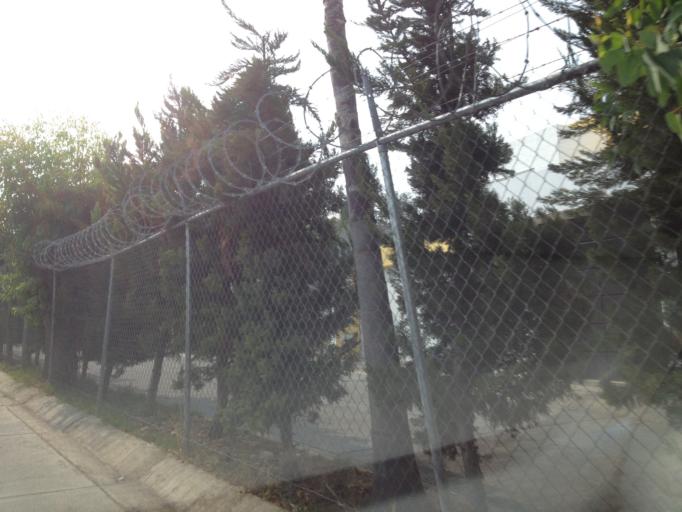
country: MX
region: Michoacan
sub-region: Morelia
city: Morelos
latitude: 19.6718
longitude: -101.2296
